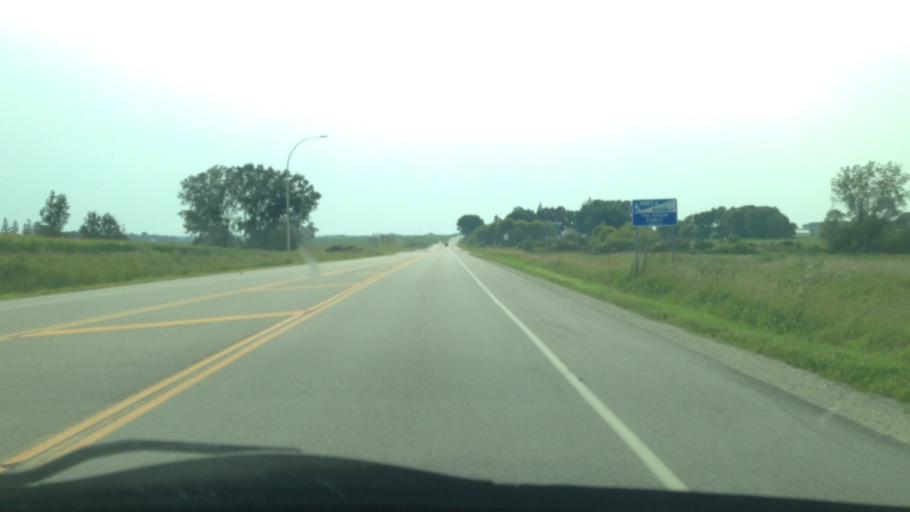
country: US
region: Minnesota
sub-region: Olmsted County
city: Eyota
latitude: 43.9991
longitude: -92.2509
